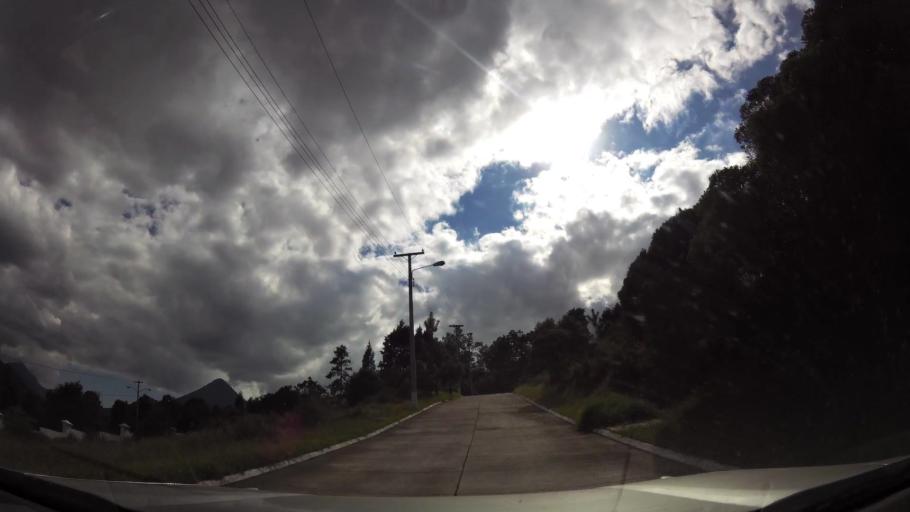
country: GT
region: Quetzaltenango
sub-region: Municipio de La Esperanza
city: La Esperanza
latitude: 14.8347
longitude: -91.5588
